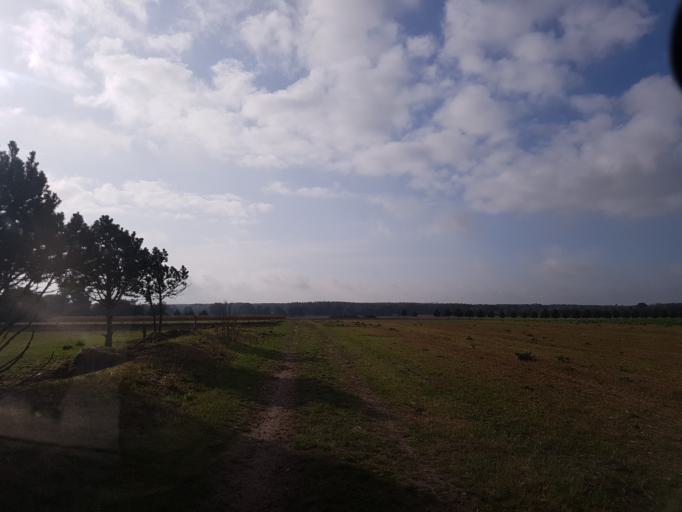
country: DE
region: Brandenburg
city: Finsterwalde
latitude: 51.6273
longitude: 13.7648
